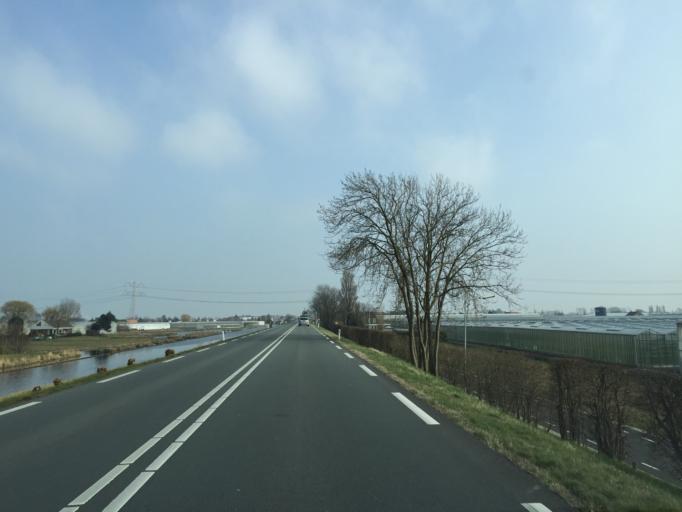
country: NL
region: South Holland
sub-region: Gemeente Westland
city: Naaldwijk
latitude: 51.9746
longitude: 4.1937
